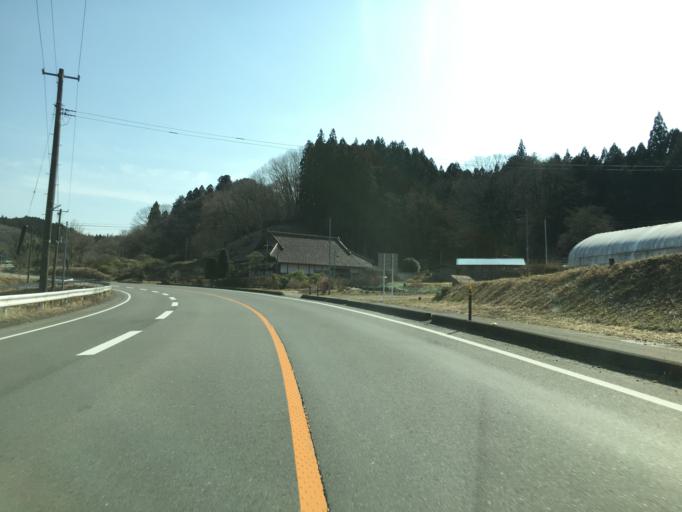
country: JP
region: Ibaraki
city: Daigo
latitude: 36.8038
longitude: 140.4701
